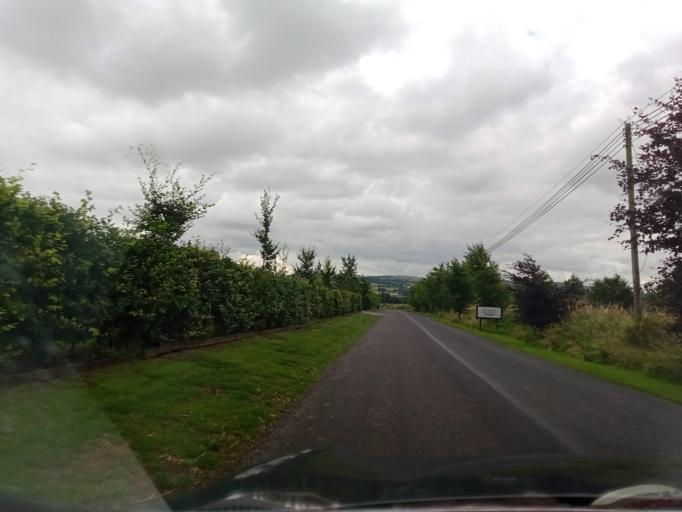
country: IE
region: Leinster
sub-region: Laois
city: Stradbally
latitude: 52.9633
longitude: -7.1954
